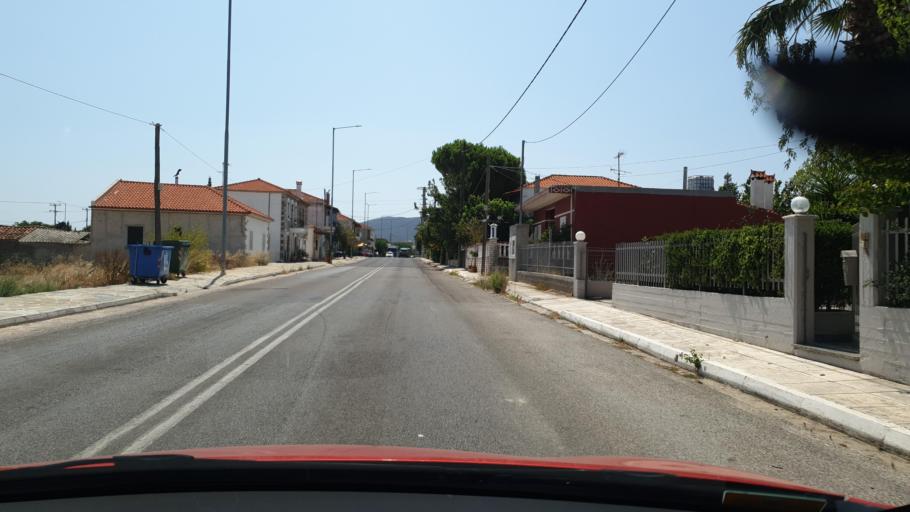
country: GR
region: Central Greece
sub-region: Nomos Evvoias
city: Aliveri
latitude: 38.4072
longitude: 24.1086
